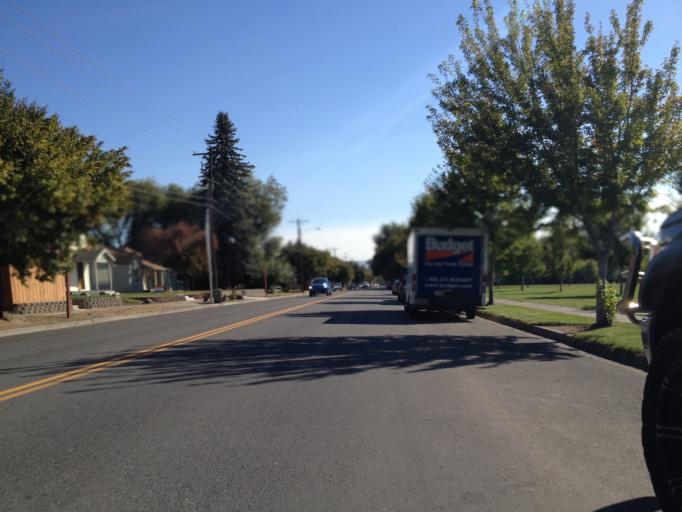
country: US
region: Washington
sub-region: Kittitas County
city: Ellensburg
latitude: 47.0061
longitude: -120.5320
